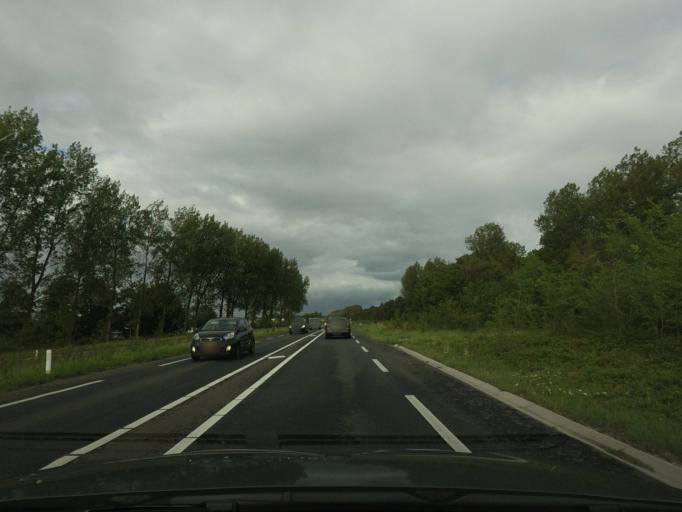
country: NL
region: South Holland
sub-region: Gemeente Noordwijkerhout
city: Noordwijkerhout
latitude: 52.2713
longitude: 4.5044
